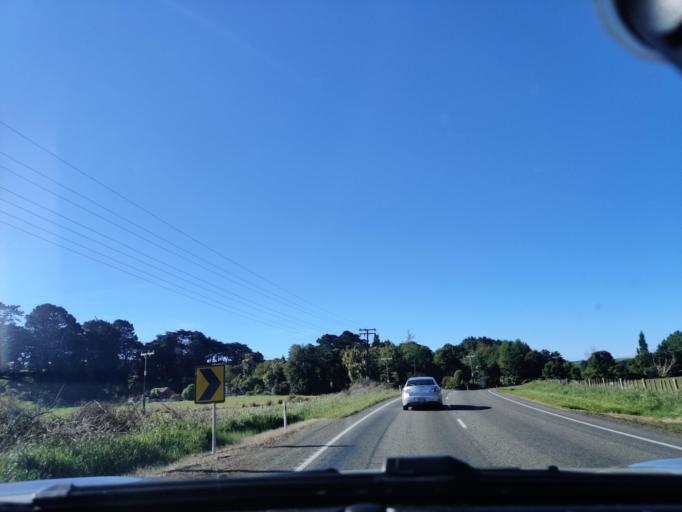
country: NZ
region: Manawatu-Wanganui
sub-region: Palmerston North City
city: Palmerston North
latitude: -40.6057
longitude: 175.7115
